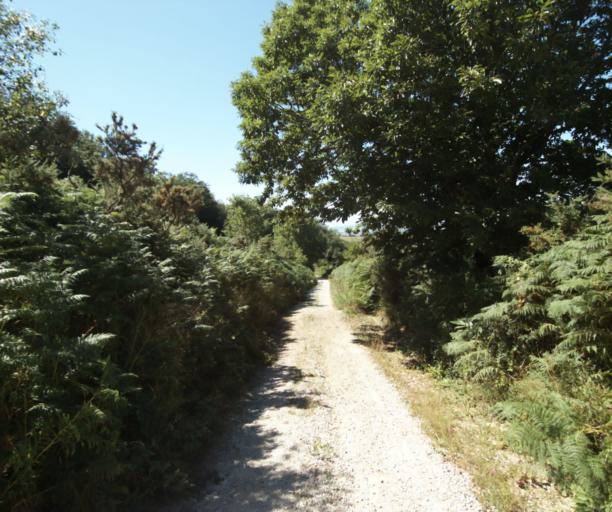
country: FR
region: Midi-Pyrenees
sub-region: Departement du Tarn
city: Soreze
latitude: 43.4420
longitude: 2.0985
